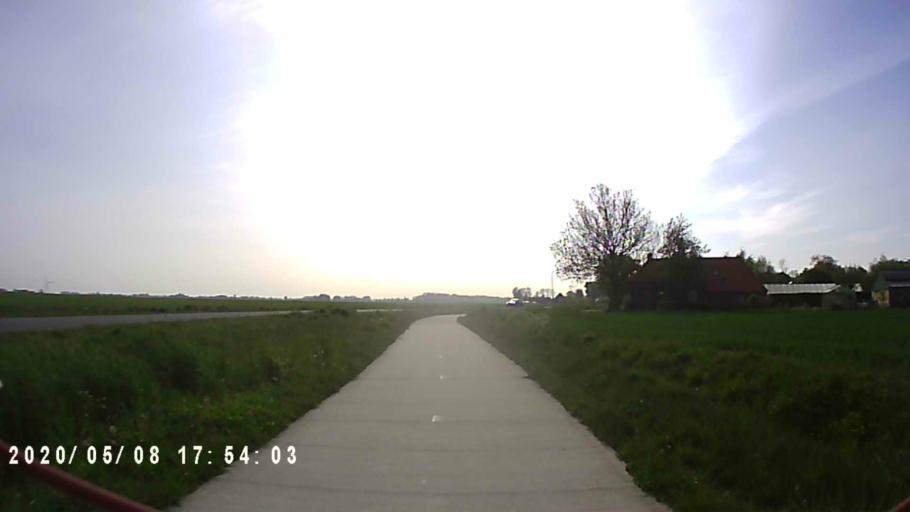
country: NL
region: Groningen
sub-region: Gemeente Winsum
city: Winsum
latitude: 53.3645
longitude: 6.4991
